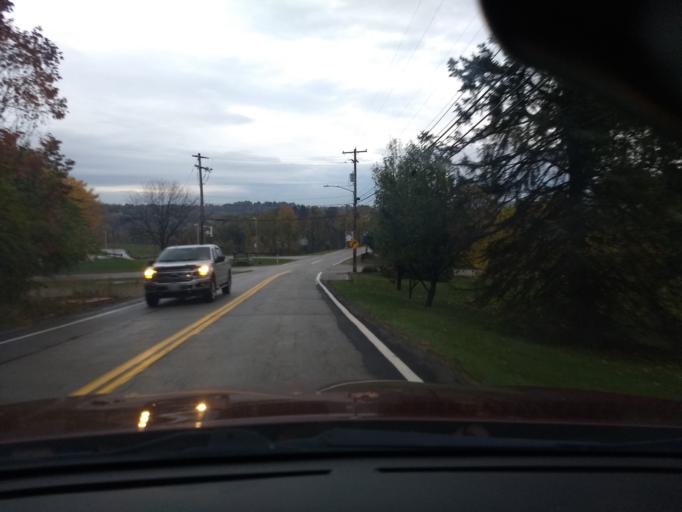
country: US
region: Pennsylvania
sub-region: Allegheny County
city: Jefferson Hills
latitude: 40.2962
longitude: -79.9306
